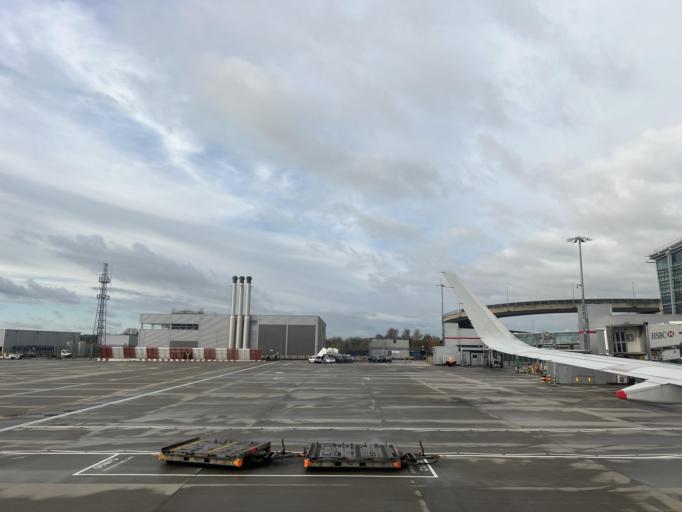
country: GB
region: England
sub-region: Buckinghamshire
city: Iver
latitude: 51.4691
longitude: -0.4872
